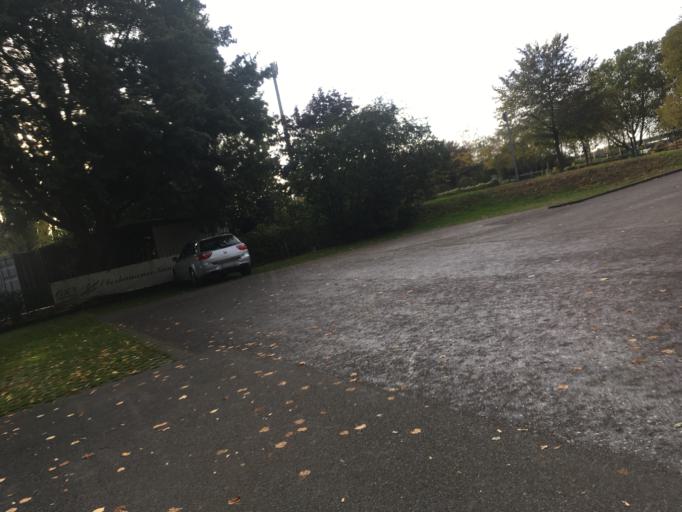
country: DE
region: North Rhine-Westphalia
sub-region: Regierungsbezirk Dusseldorf
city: Oberhausen
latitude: 51.4927
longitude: 6.8533
